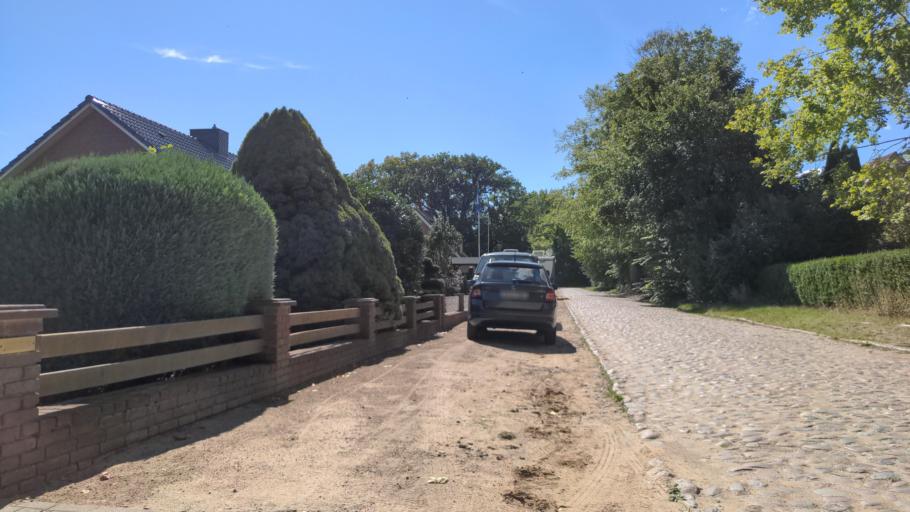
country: DE
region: Schleswig-Holstein
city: Beschendorf
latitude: 54.2100
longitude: 10.8581
